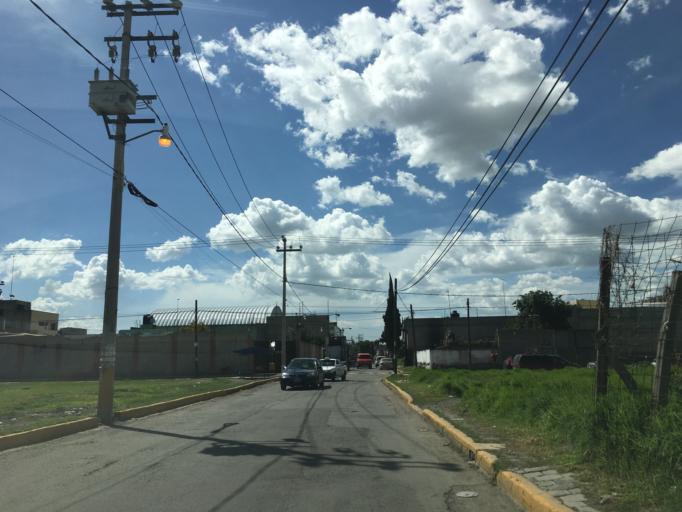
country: MX
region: Mexico
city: Ecatepec
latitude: 19.6141
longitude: -99.0545
